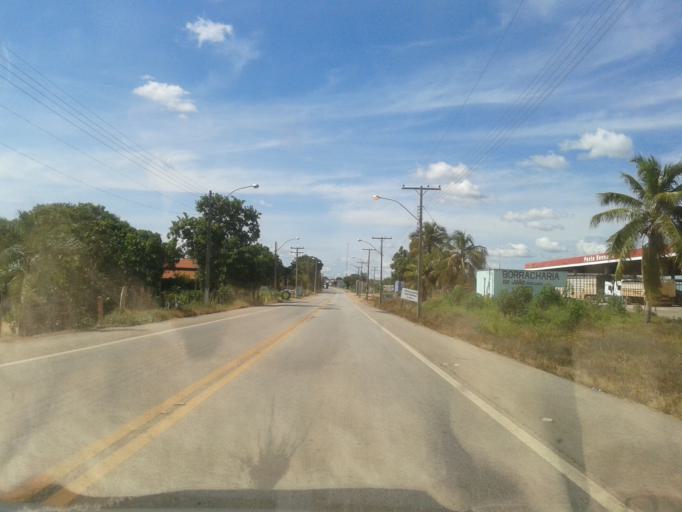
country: BR
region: Goias
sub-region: Itapuranga
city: Itapuranga
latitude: -15.4551
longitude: -50.3593
